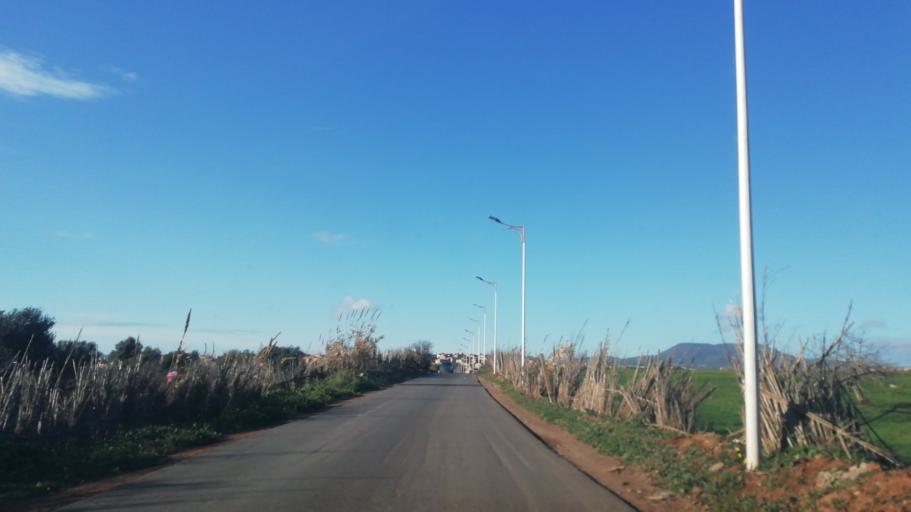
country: DZ
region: Oran
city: Sidi ech Chahmi
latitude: 35.6830
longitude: -0.4932
